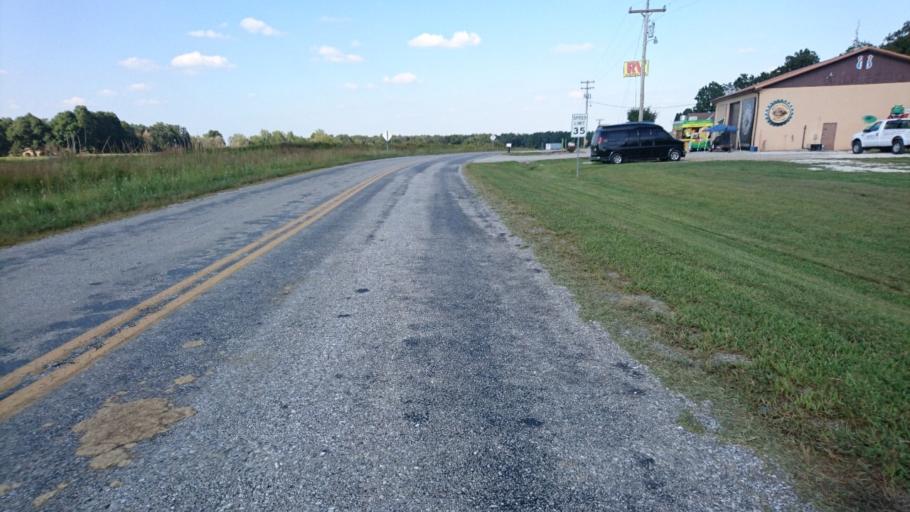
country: US
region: Missouri
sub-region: Laclede County
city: Lebanon
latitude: 37.5993
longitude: -92.7134
